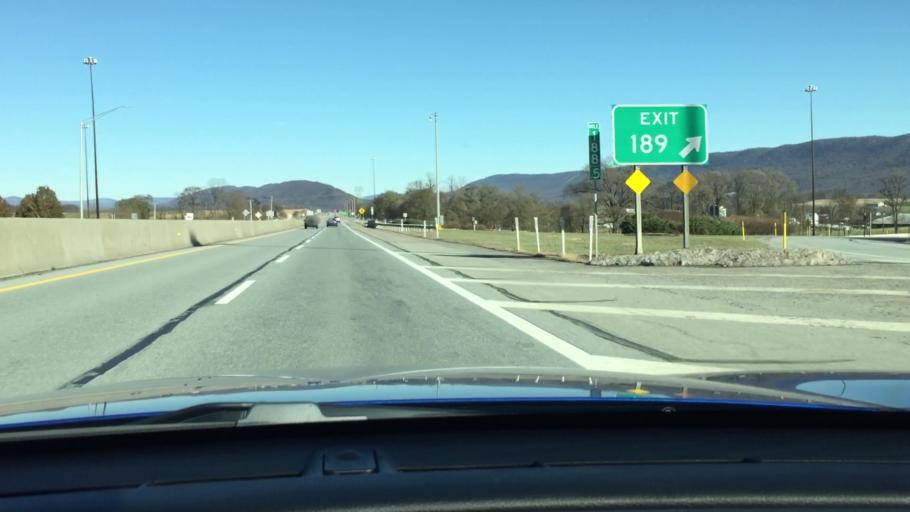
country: US
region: Pennsylvania
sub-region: Franklin County
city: Doylestown
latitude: 40.0959
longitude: -77.8169
